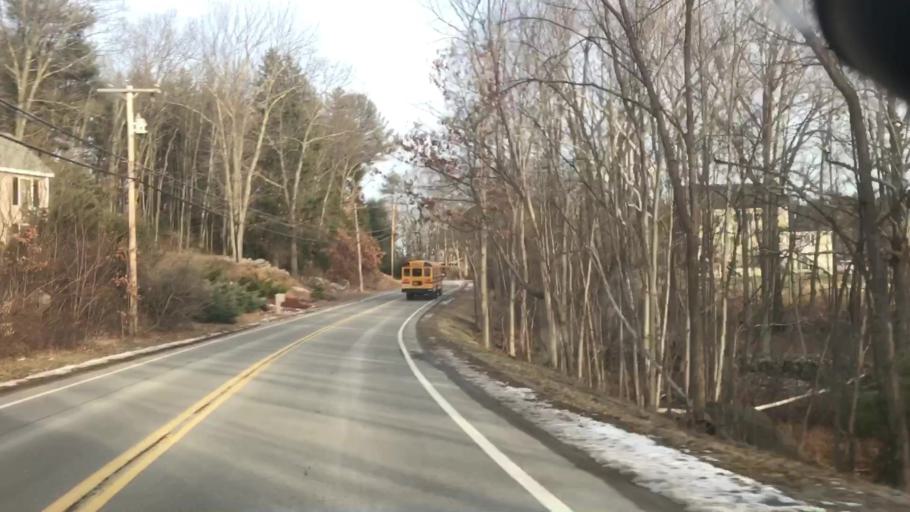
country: US
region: New Hampshire
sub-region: Hillsborough County
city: Bedford
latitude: 42.9363
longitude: -71.5479
